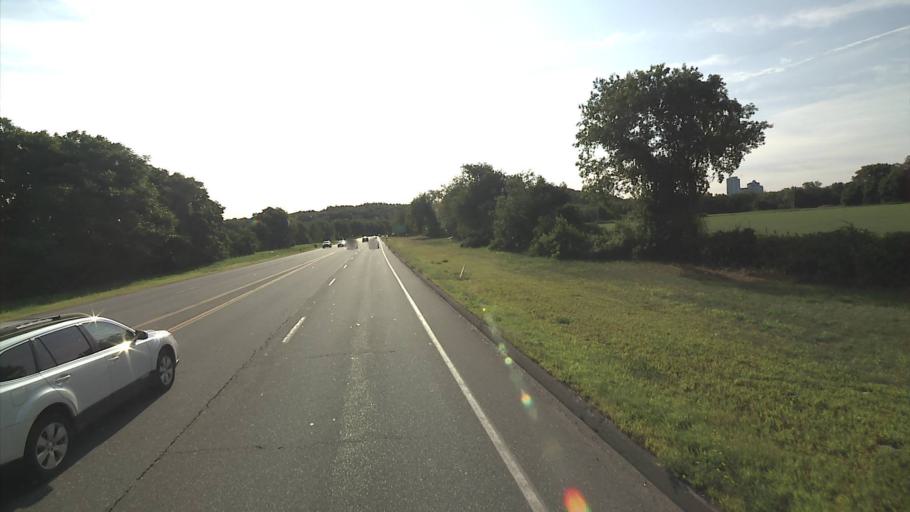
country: US
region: Connecticut
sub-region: New London County
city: Preston City
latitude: 41.4882
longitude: -71.9799
